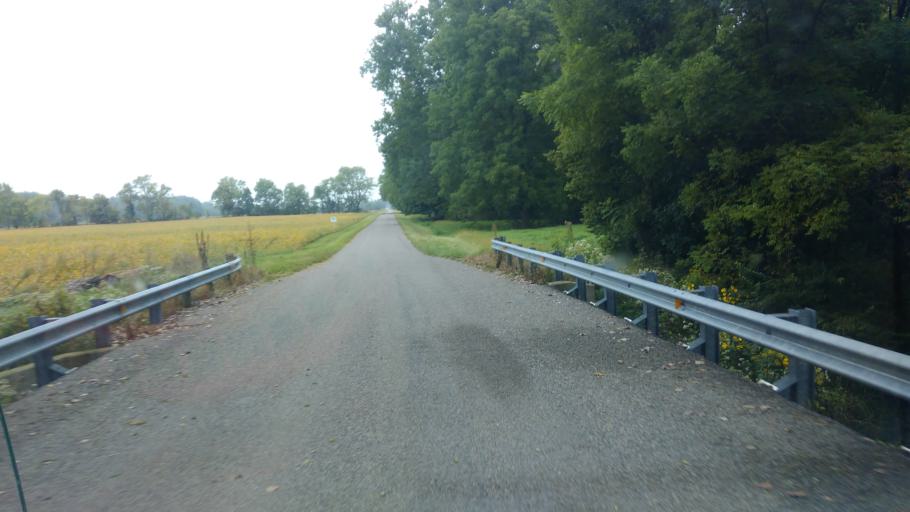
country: US
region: Ohio
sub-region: Logan County
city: Northwood
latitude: 40.4756
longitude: -83.6179
